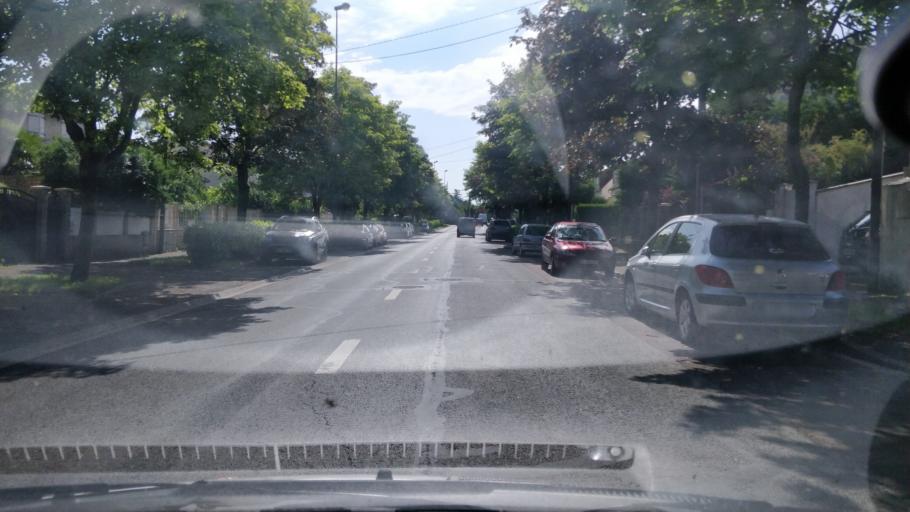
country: FR
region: Ile-de-France
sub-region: Departement de Seine-Saint-Denis
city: Montfermeil
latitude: 48.8944
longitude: 2.5762
